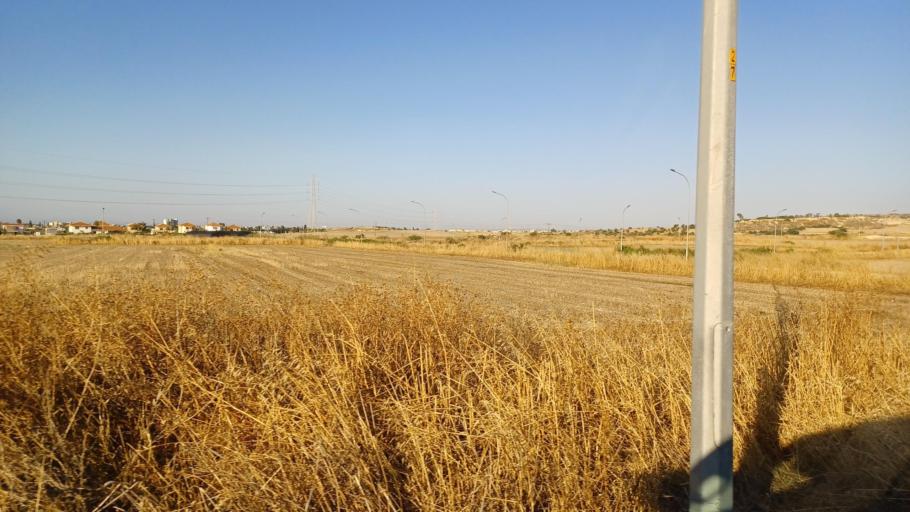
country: CY
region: Larnaka
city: Voroklini
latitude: 34.9907
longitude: 33.6783
